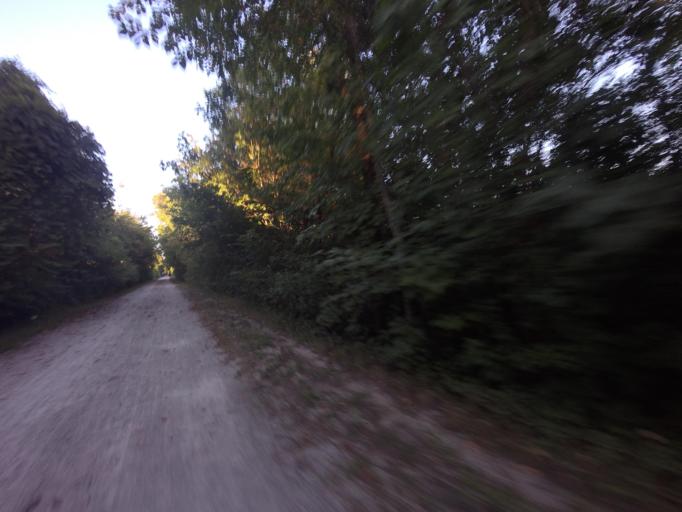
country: CA
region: Ontario
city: Brampton
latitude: 43.8809
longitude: -79.8497
